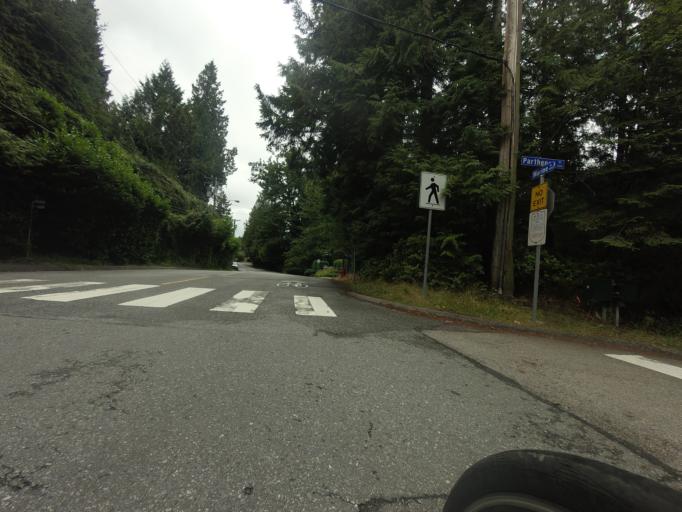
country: CA
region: British Columbia
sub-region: Greater Vancouver Regional District
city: Bowen Island
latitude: 49.3512
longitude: -123.2663
